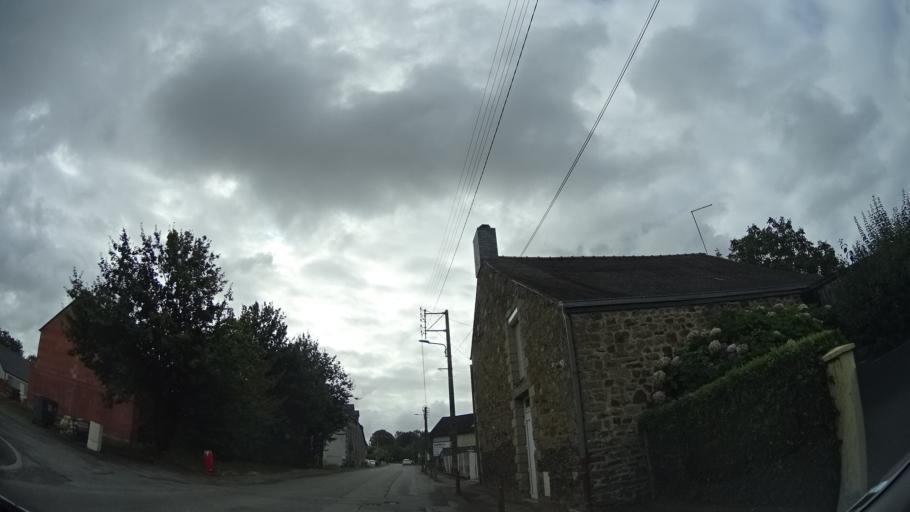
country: FR
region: Brittany
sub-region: Departement d'Ille-et-Vilaine
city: Montreuil-sur-Ille
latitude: 48.3057
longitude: -1.6669
